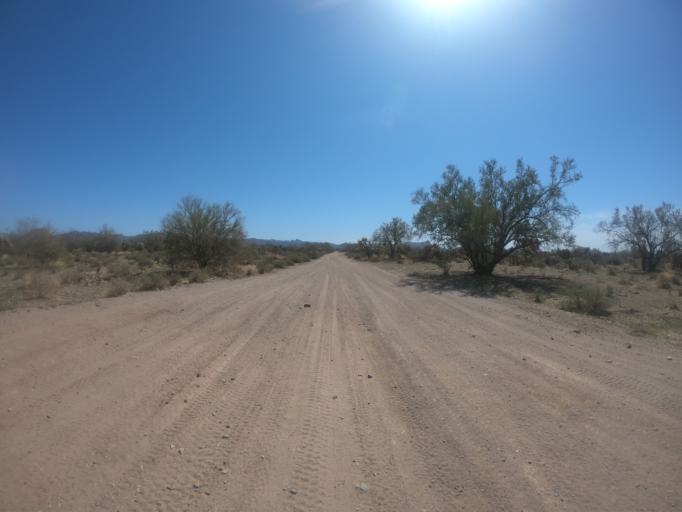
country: US
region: Arizona
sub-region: Pinal County
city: Gold Camp
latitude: 33.2353
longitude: -111.3041
